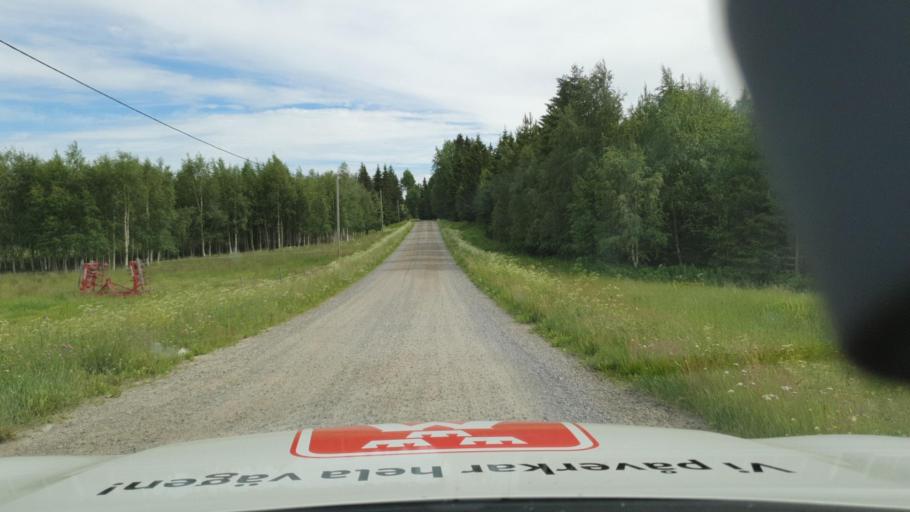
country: SE
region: Vaesterbotten
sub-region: Robertsfors Kommun
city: Robertsfors
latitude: 64.3940
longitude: 21.0202
